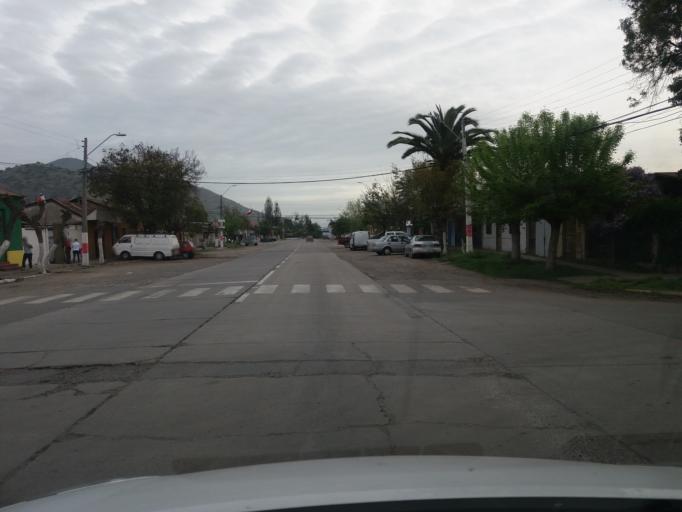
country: CL
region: Valparaiso
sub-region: Provincia de Quillota
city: Hacienda La Calera
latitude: -32.7783
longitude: -71.1820
